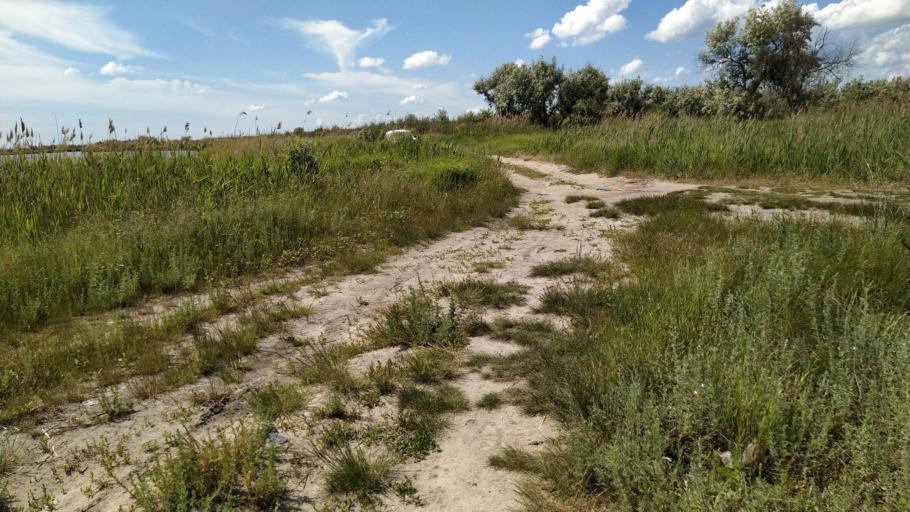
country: RU
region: Rostov
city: Bataysk
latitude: 47.1347
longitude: 39.6760
